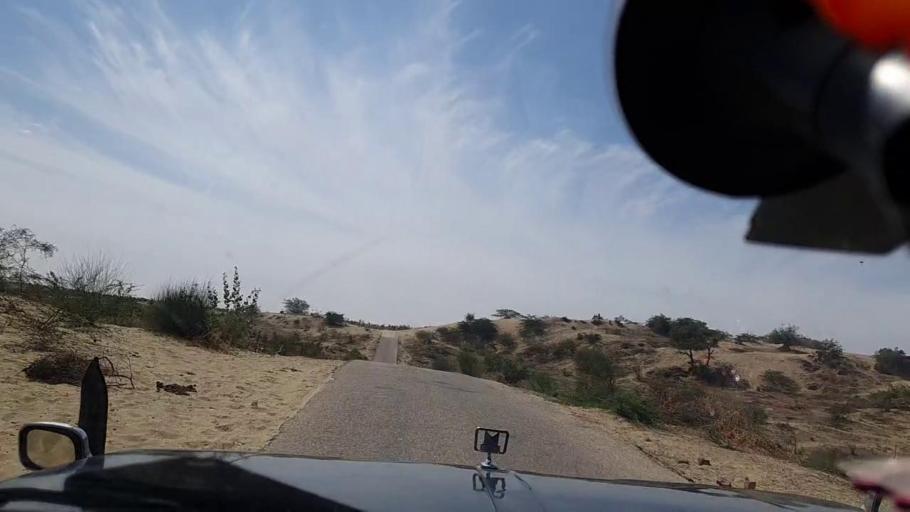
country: PK
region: Sindh
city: Diplo
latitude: 24.4000
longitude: 69.5886
